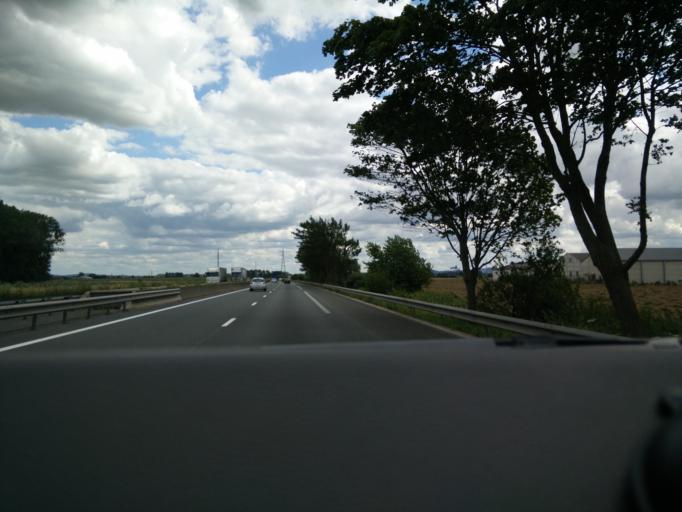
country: FR
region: Nord-Pas-de-Calais
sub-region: Departement du Nord
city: Quaedypre
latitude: 50.9184
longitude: 2.4785
